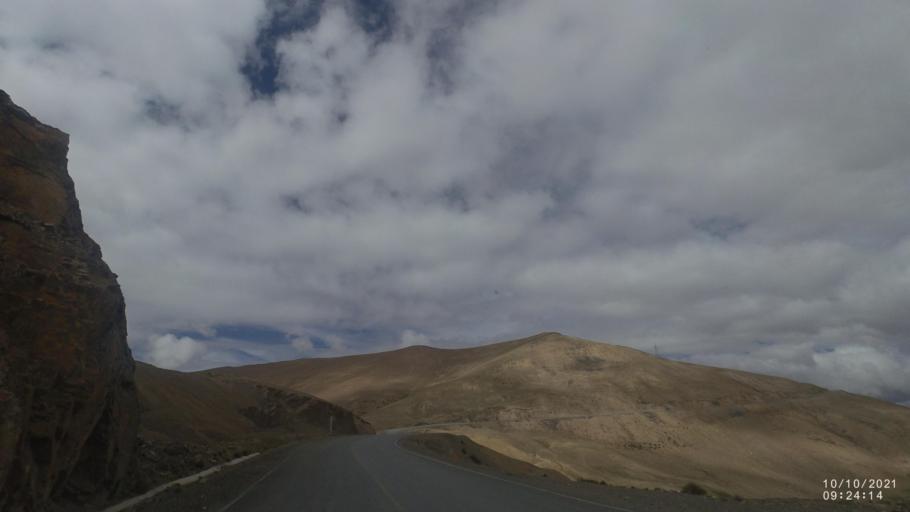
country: BO
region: La Paz
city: Quime
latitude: -17.0879
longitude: -67.3086
